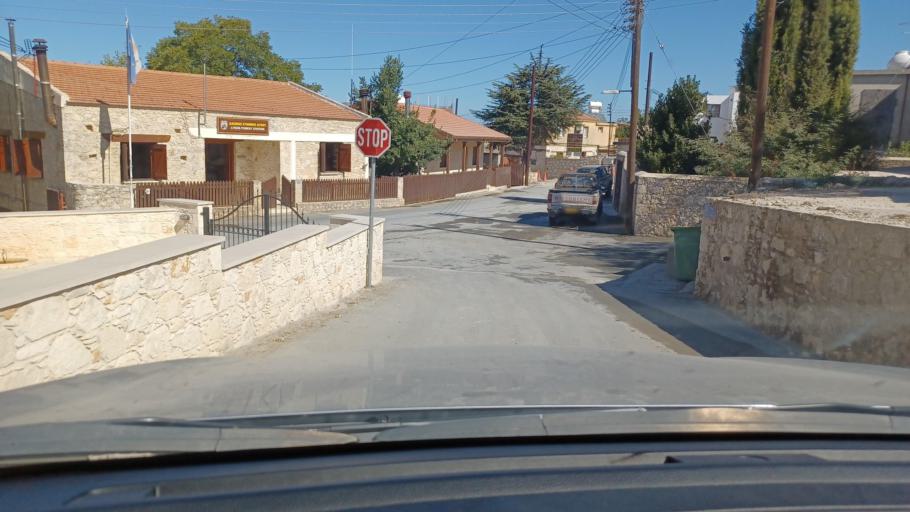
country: CY
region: Pafos
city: Polis
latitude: 34.9937
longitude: 32.5113
